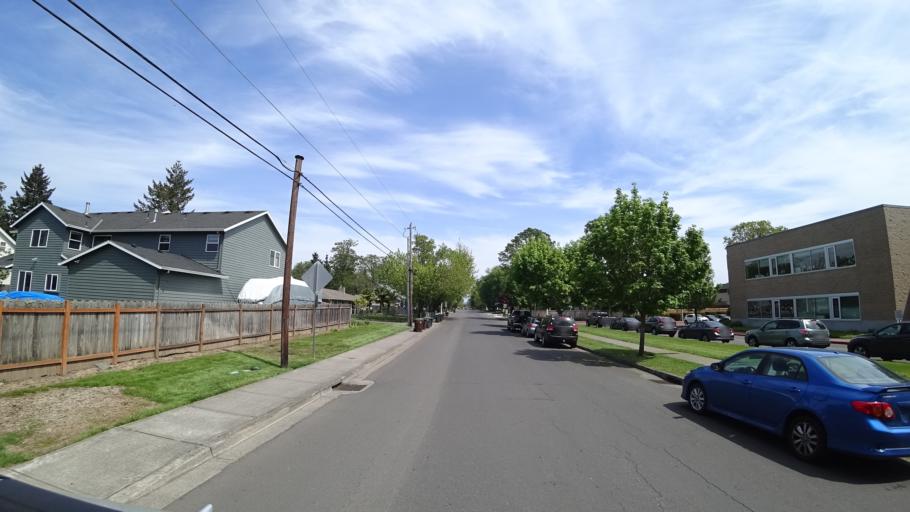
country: US
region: Oregon
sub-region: Washington County
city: Aloha
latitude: 45.5123
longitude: -122.9208
